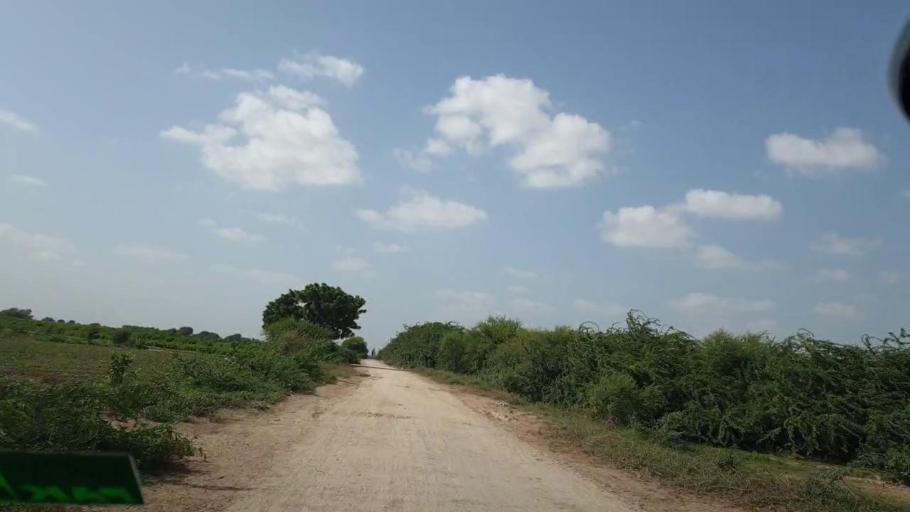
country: PK
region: Sindh
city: Naukot
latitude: 24.6481
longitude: 69.2213
